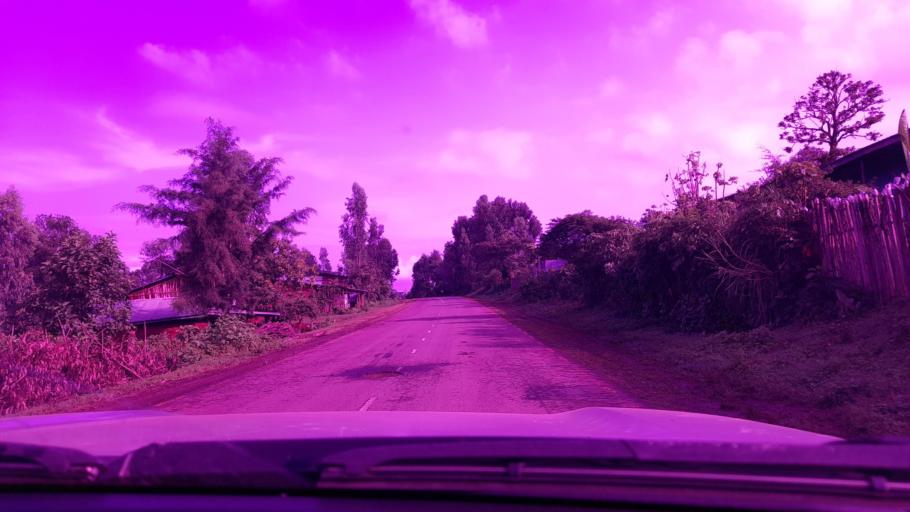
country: ET
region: Oromiya
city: Bedele
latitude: 8.1812
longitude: 36.4546
